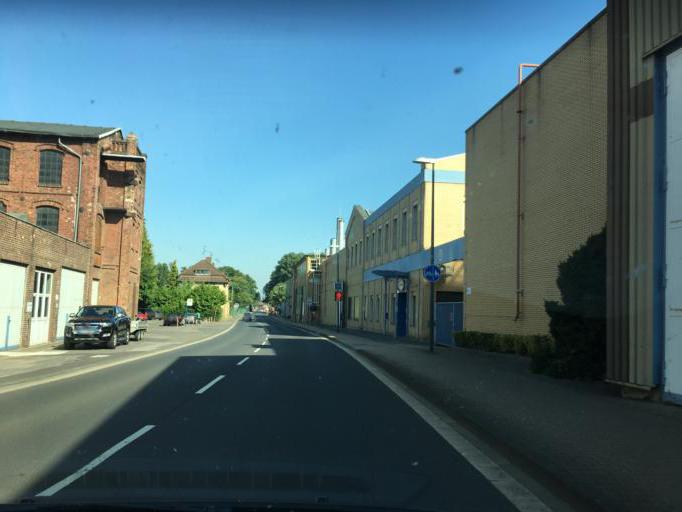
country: DE
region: North Rhine-Westphalia
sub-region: Regierungsbezirk Koln
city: Dueren
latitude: 50.8115
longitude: 6.4543
